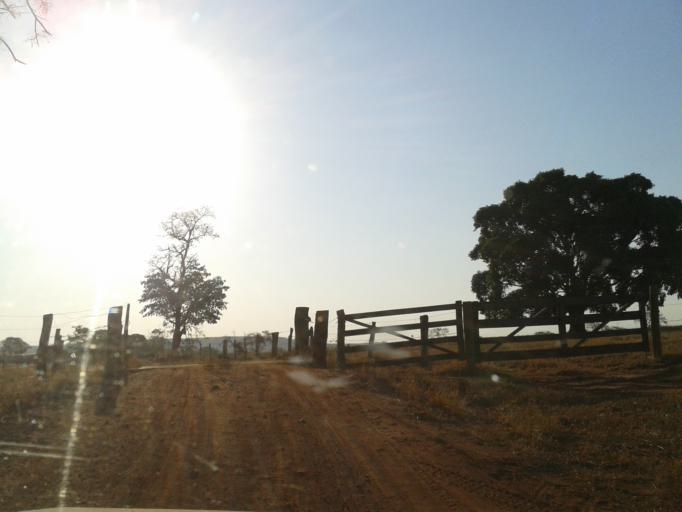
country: BR
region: Minas Gerais
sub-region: Ituiutaba
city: Ituiutaba
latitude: -19.2455
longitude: -49.5870
